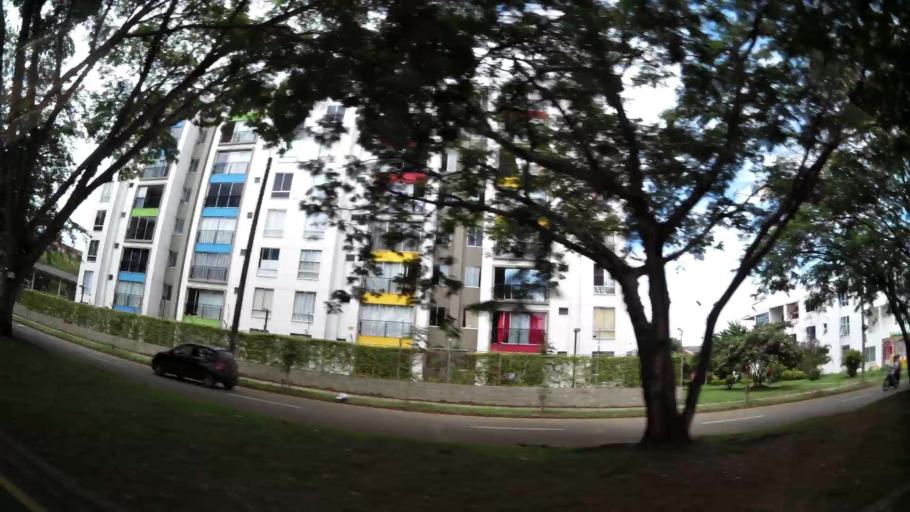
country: CO
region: Valle del Cauca
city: Cali
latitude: 3.3838
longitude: -76.5156
